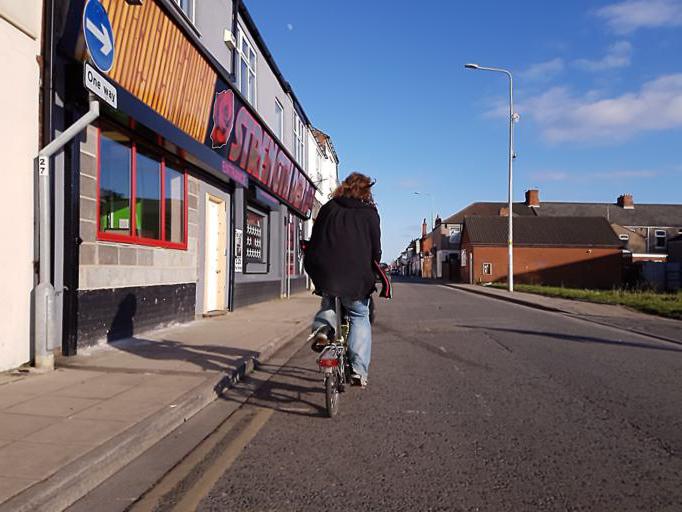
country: GB
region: England
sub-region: North East Lincolnshire
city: Grimsby
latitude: 53.5657
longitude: -0.0774
